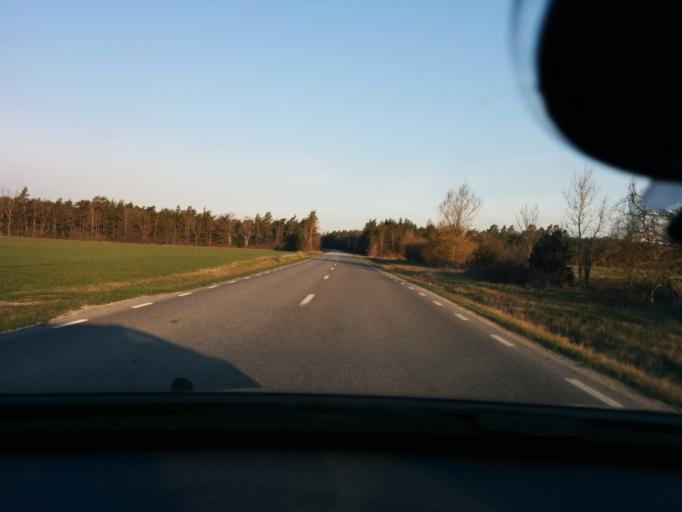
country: SE
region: Gotland
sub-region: Gotland
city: Visby
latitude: 57.6390
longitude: 18.5035
